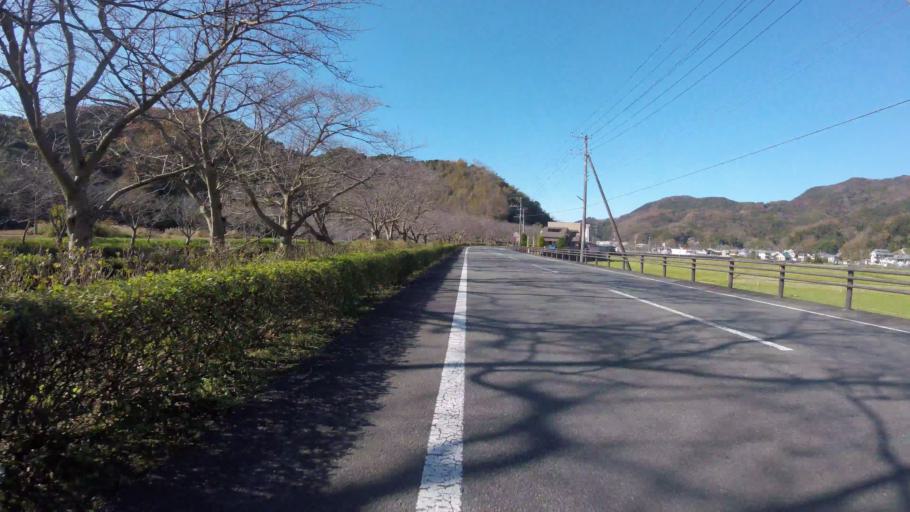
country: JP
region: Shizuoka
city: Shimoda
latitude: 34.7521
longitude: 138.7974
